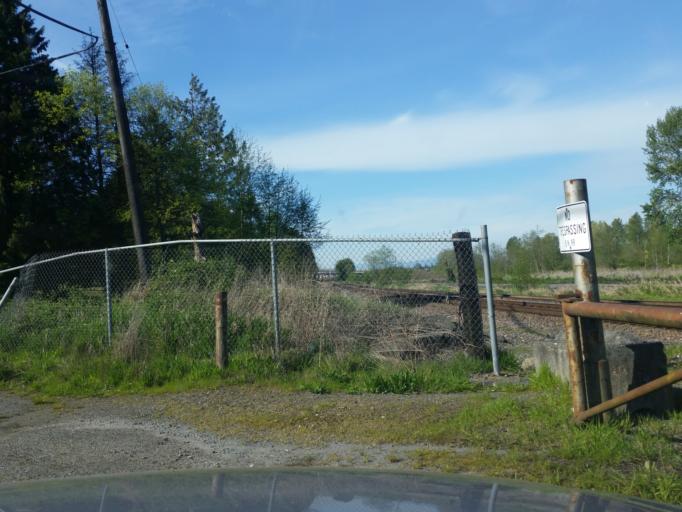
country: US
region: Washington
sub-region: Snohomish County
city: Everett
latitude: 47.9548
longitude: -122.1952
